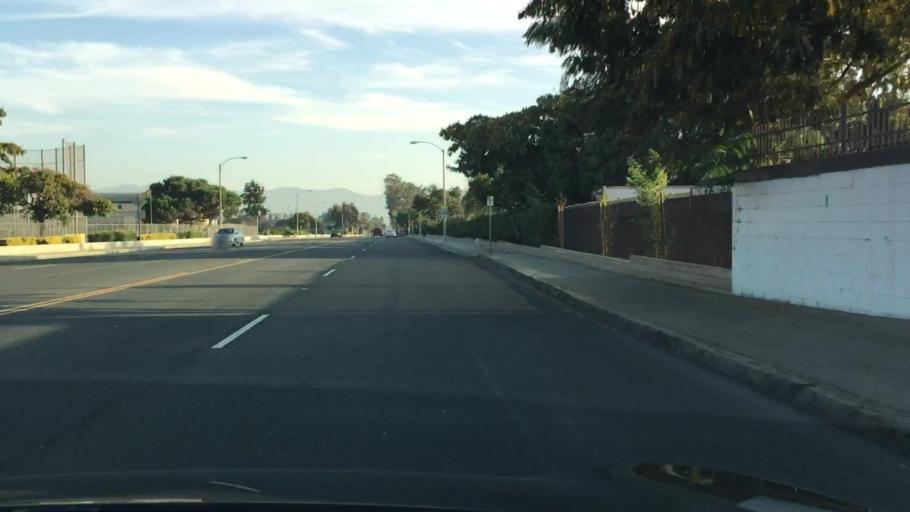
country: US
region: California
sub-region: San Bernardino County
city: Ontario
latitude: 34.0263
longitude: -117.6416
